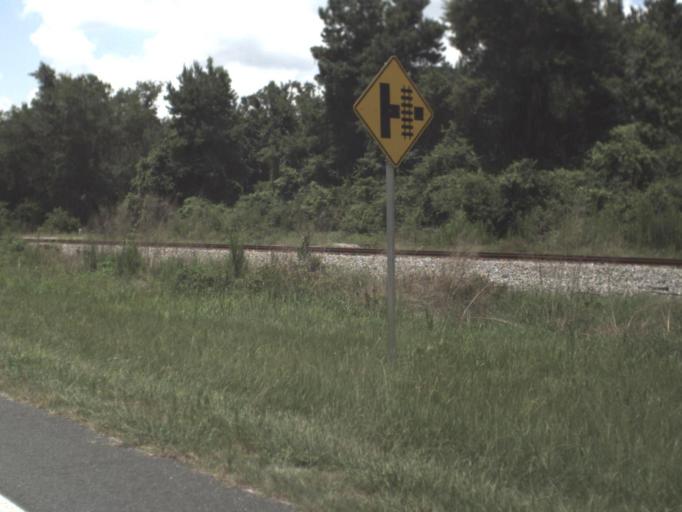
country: US
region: Florida
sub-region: Suwannee County
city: Wellborn
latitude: 30.3433
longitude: -82.7644
